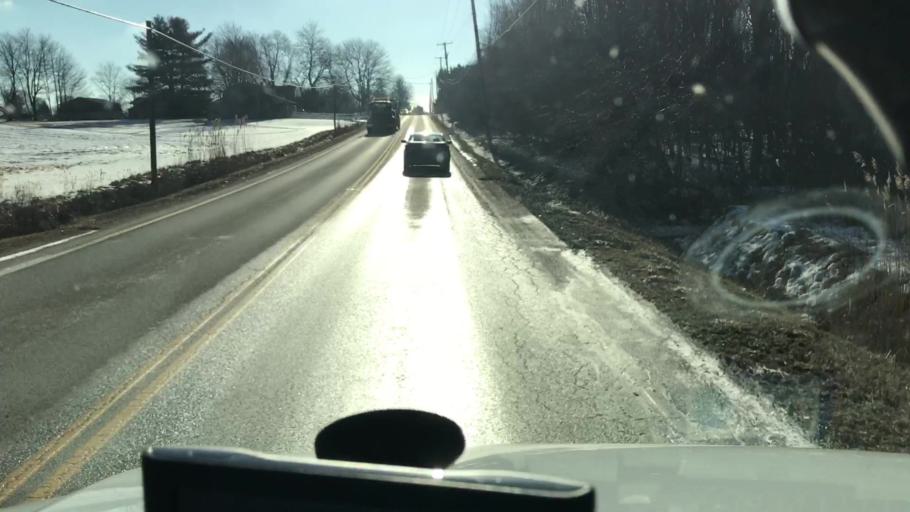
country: US
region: Ohio
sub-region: Mahoning County
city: New Middletown
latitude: 40.9264
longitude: -80.6197
